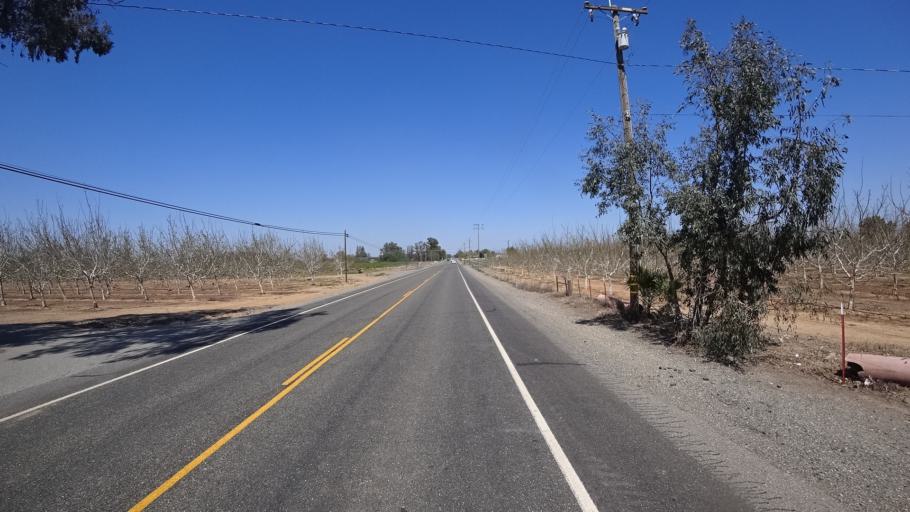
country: US
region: California
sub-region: Glenn County
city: Orland
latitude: 39.7861
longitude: -122.1976
